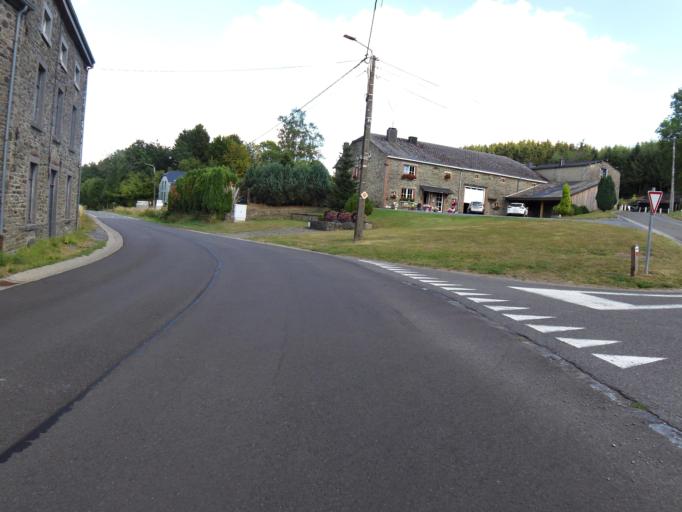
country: BE
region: Wallonia
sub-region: Province de Namur
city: Bievre
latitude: 49.8935
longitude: 5.0104
